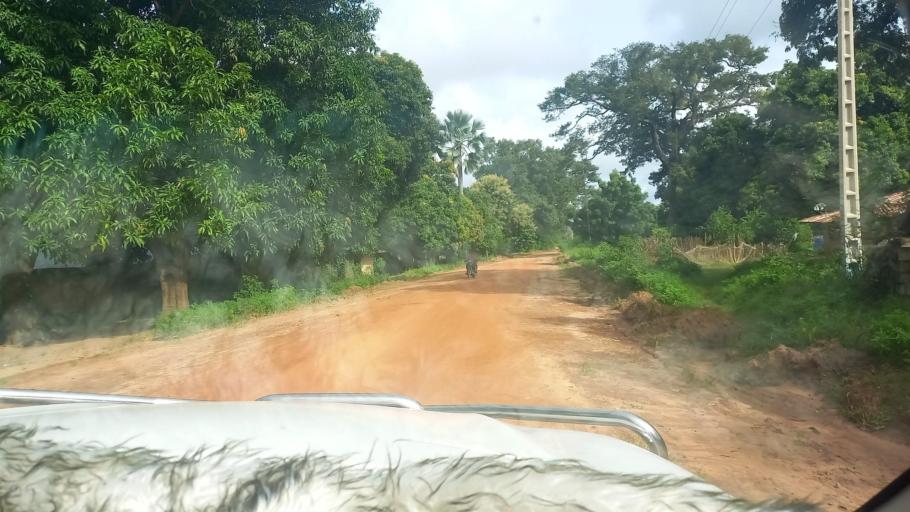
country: SN
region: Ziguinchor
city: Ziguinchor
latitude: 12.6645
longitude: -16.2652
